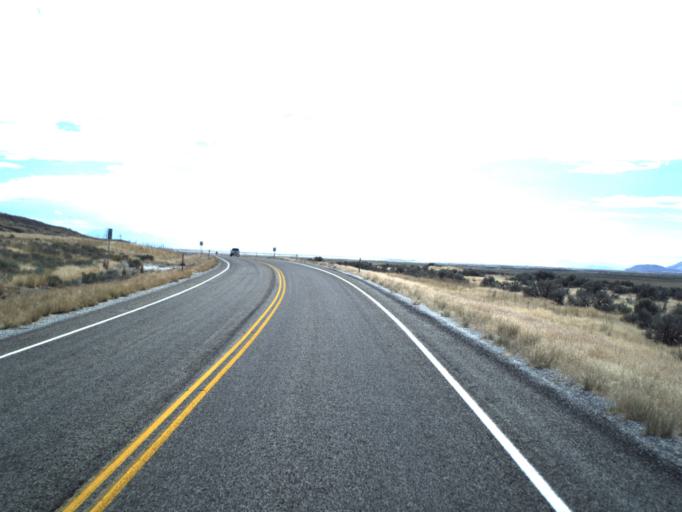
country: US
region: Utah
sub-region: Box Elder County
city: Tremonton
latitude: 41.6547
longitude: -112.4398
